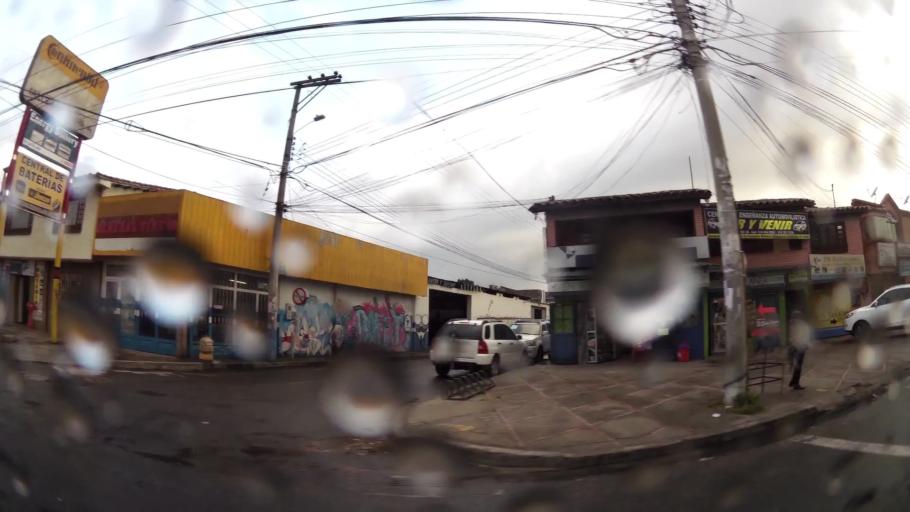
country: CO
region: Cundinamarca
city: Chia
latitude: 4.8635
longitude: -74.0491
